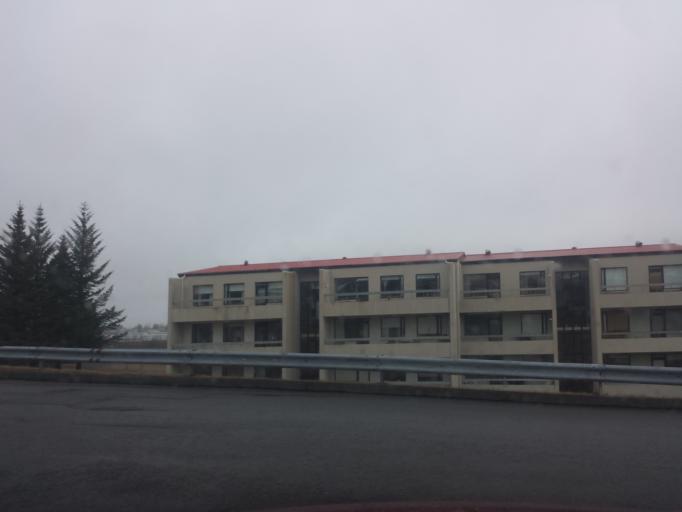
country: IS
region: Capital Region
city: Reykjavik
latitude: 64.1132
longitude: -21.8596
